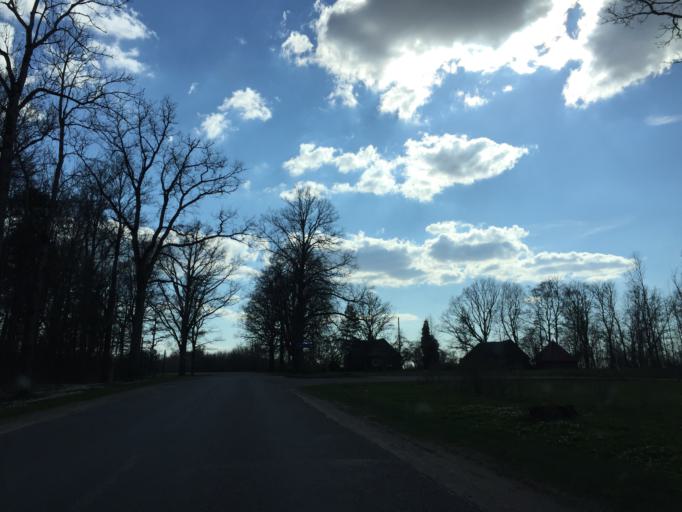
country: LV
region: Krimulda
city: Ragana
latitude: 57.3340
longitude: 24.6459
